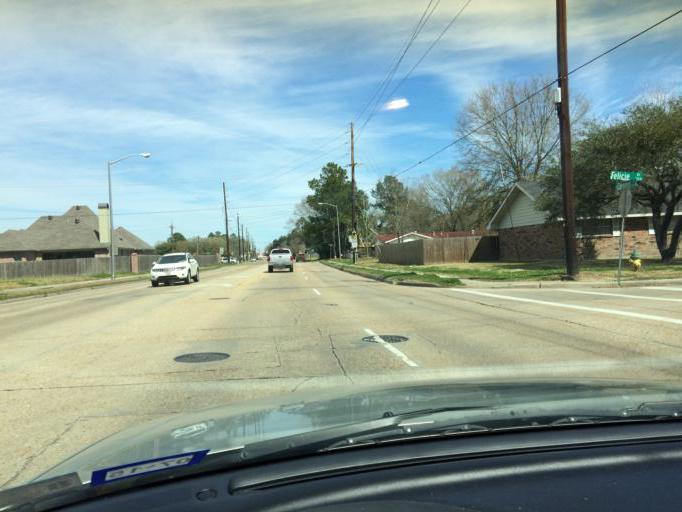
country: US
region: Louisiana
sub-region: Lafayette Parish
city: Lafayette
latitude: 30.2050
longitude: -92.0601
